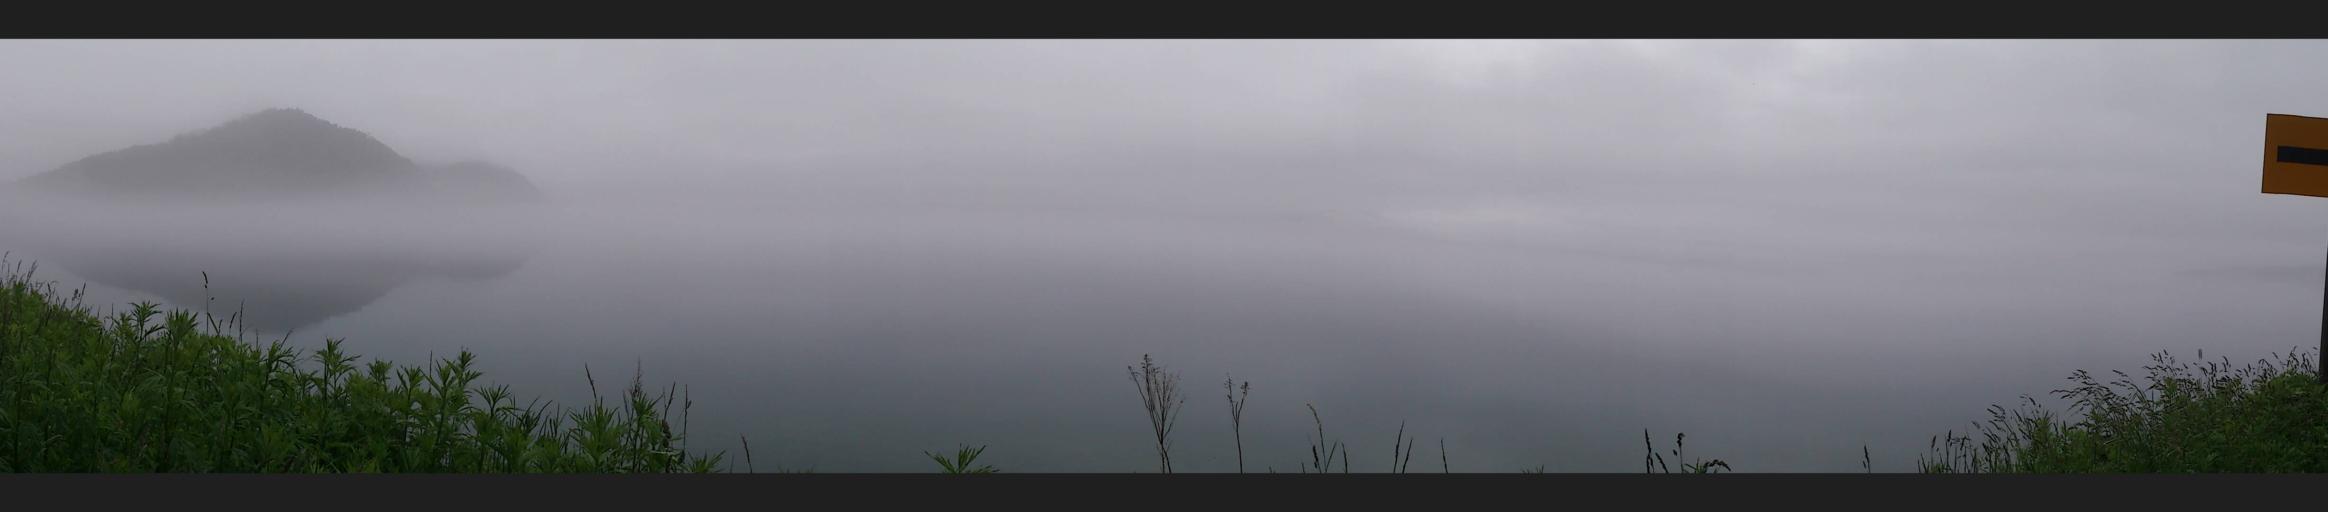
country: JP
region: Hokkaido
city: Shiraoi
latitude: 42.7771
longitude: 141.3949
